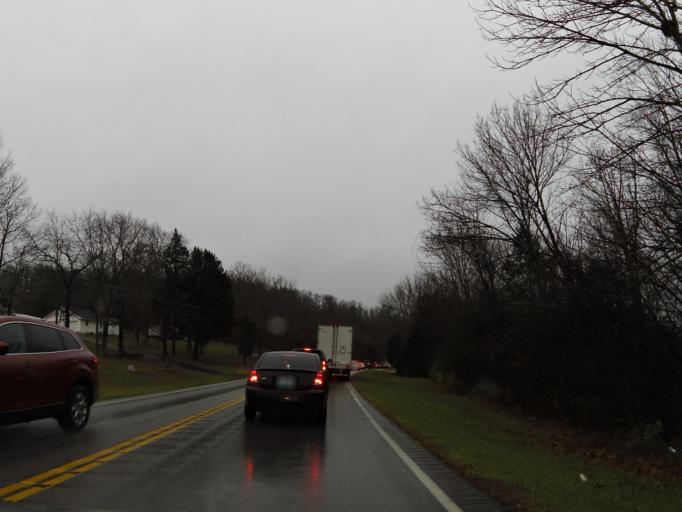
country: US
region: Kentucky
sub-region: Rockcastle County
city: Mount Vernon
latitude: 37.4155
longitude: -84.3332
